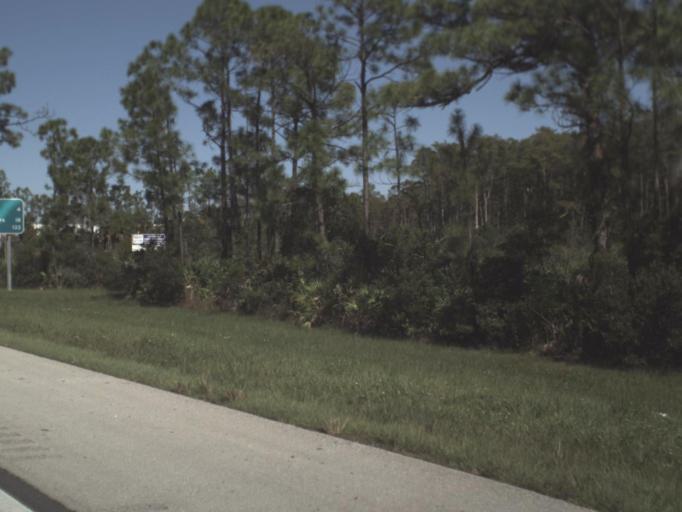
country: US
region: Florida
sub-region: Lee County
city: Gateway
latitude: 26.5605
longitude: -81.7939
